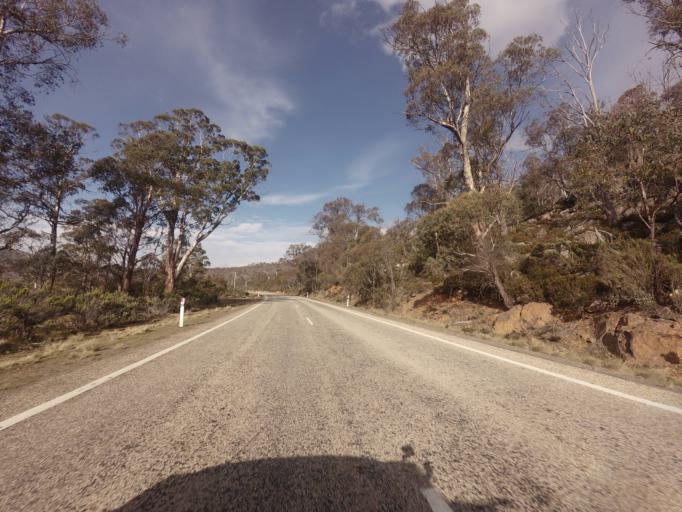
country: AU
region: Tasmania
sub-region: Meander Valley
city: Deloraine
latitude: -41.9897
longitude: 146.6820
